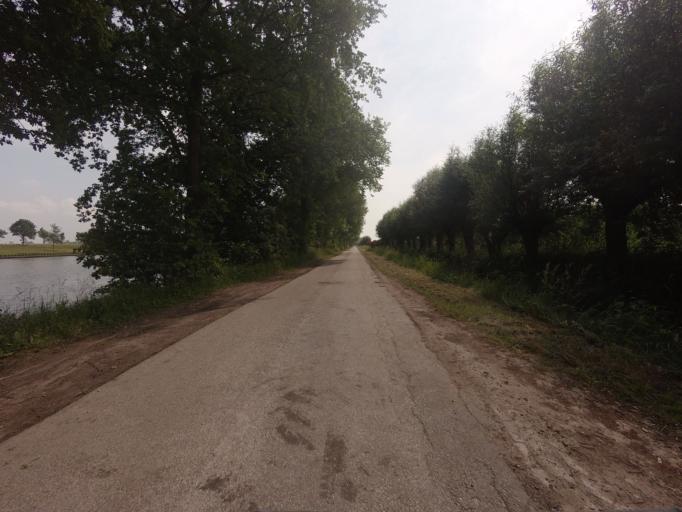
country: NL
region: Gelderland
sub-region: Gemeente Culemborg
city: Culemborg
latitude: 51.9921
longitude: 5.2321
